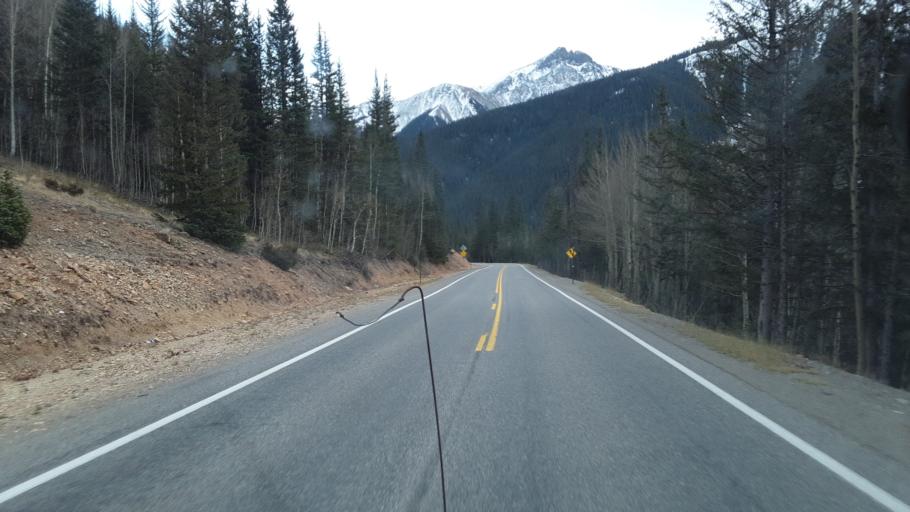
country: US
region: Colorado
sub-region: San Juan County
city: Silverton
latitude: 37.8295
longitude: -107.7233
